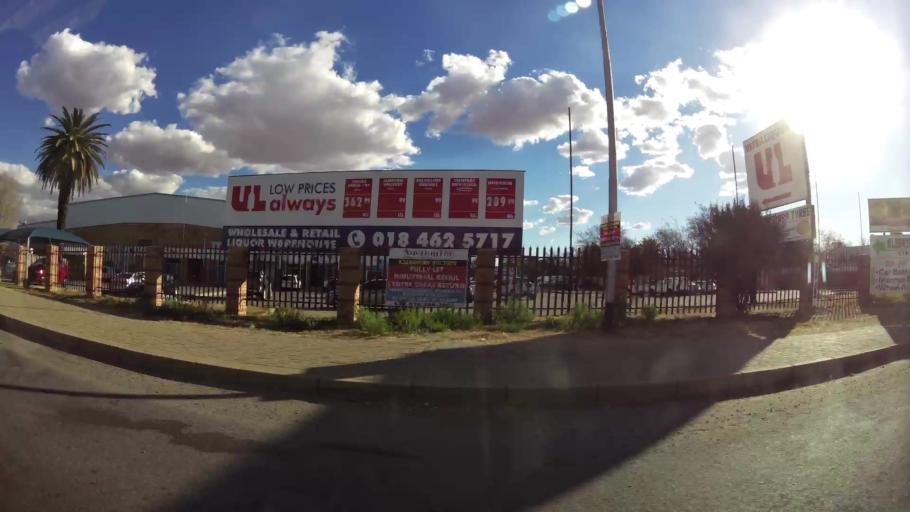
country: ZA
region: North-West
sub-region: Dr Kenneth Kaunda District Municipality
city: Klerksdorp
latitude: -26.8586
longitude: 26.6650
